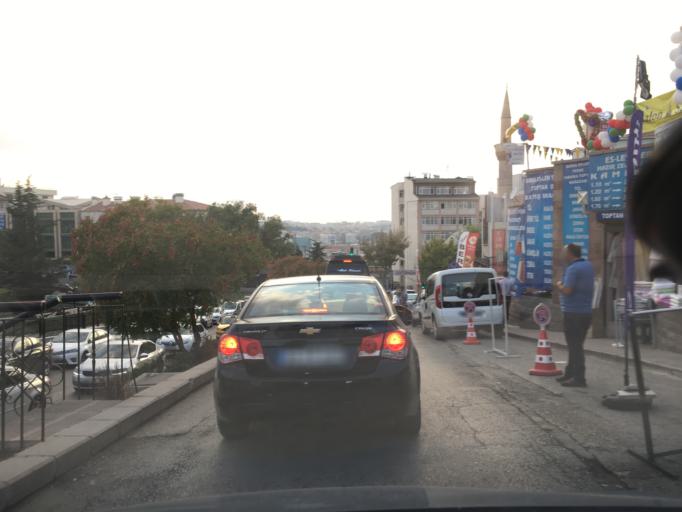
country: TR
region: Ankara
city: Cankaya
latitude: 39.9354
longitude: 32.8631
